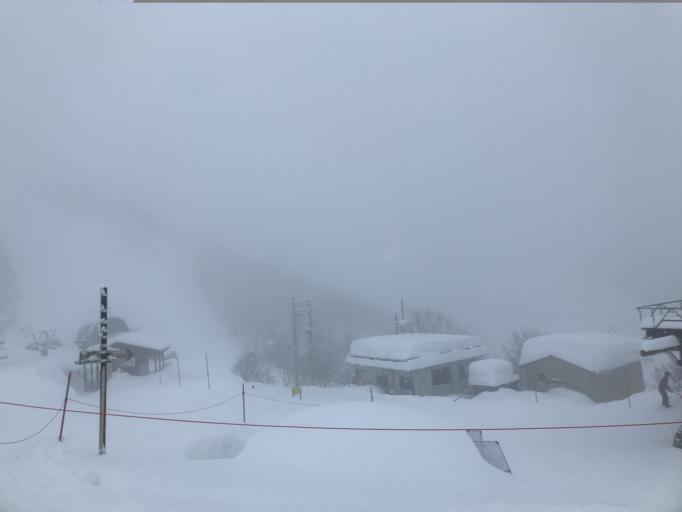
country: JP
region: Nagano
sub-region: Kitaazumi Gun
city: Hakuba
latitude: 36.6977
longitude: 137.8153
